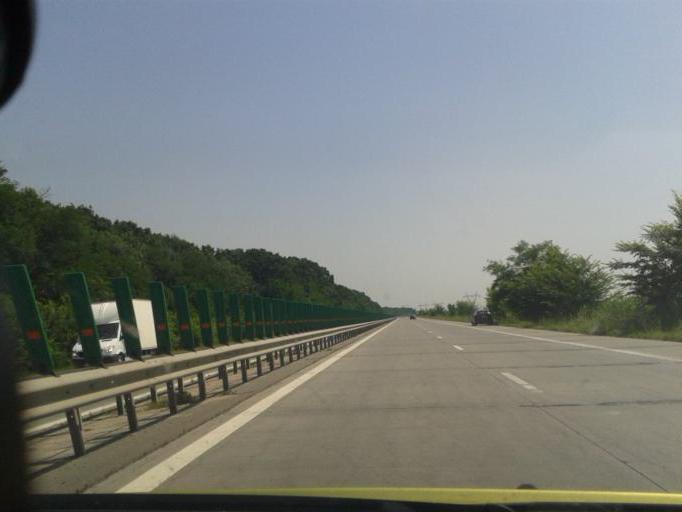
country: RO
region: Calarasi
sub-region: Comuna Belciugatele
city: Belciugatele
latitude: 44.4491
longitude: 26.4375
